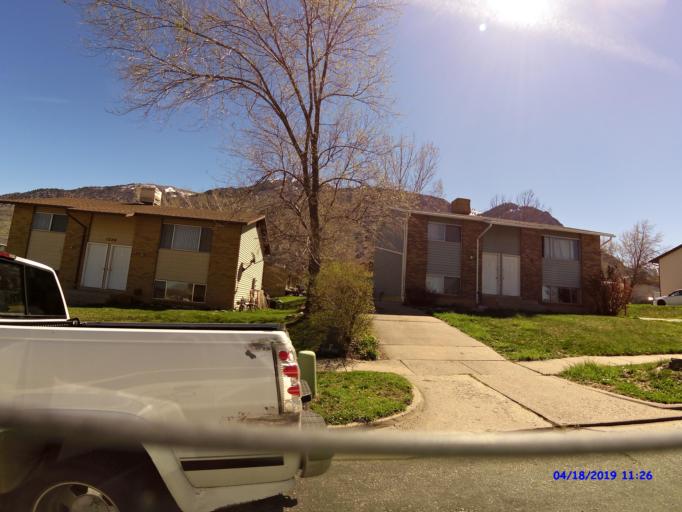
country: US
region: Utah
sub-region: Weber County
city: North Ogden
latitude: 41.2795
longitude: -111.9568
